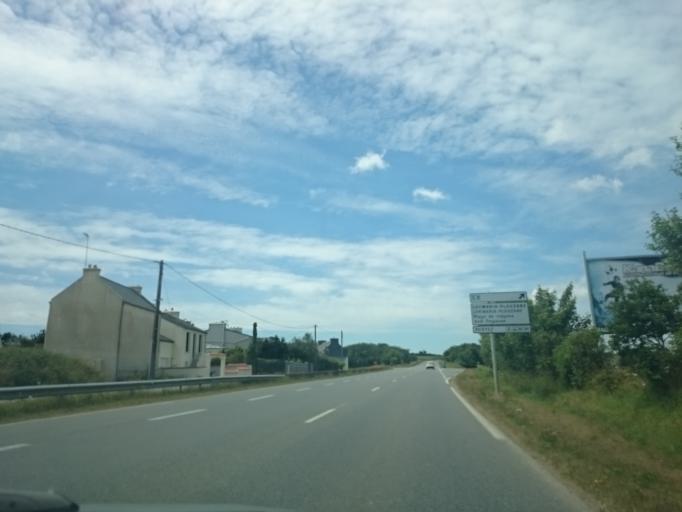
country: FR
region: Brittany
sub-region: Departement du Finistere
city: Plouzane
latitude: 48.3590
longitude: -4.6396
